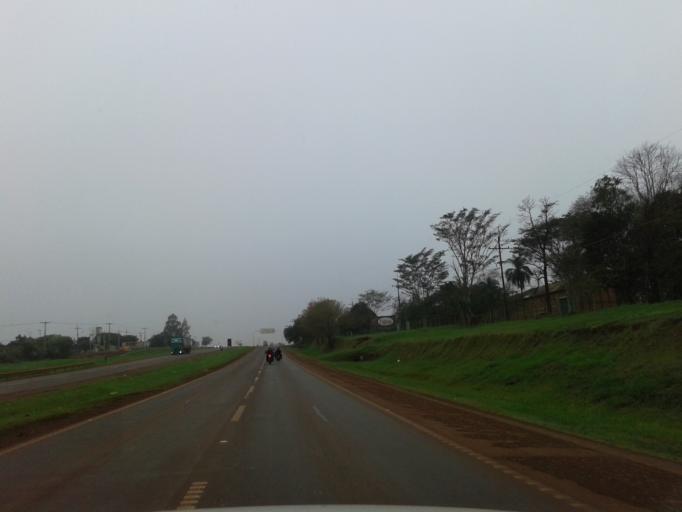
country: PY
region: Alto Parana
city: Colonia Yguazu
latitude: -25.4864
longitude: -54.8678
